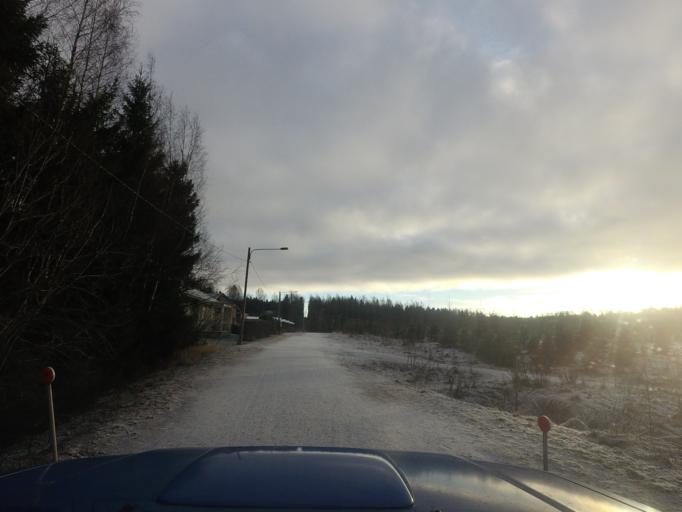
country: FI
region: Uusimaa
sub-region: Helsinki
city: Espoo
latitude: 60.1915
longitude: 24.6536
